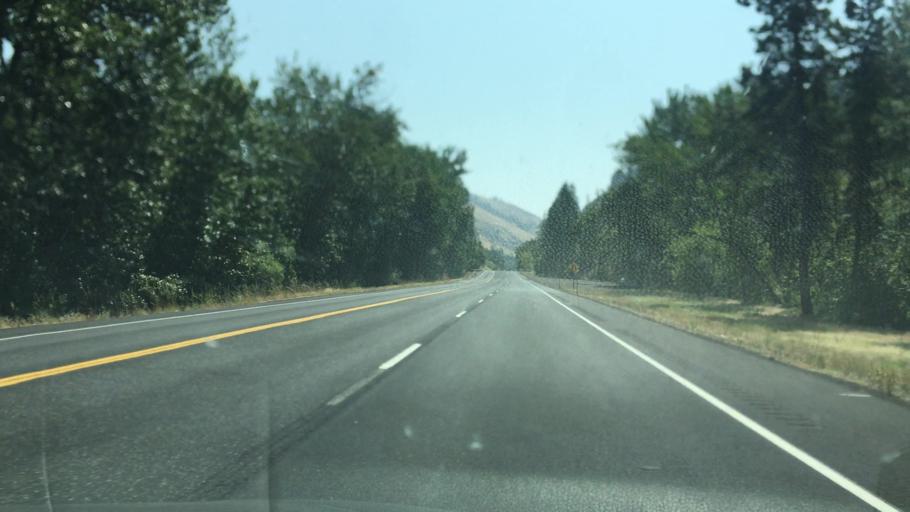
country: US
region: Idaho
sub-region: Nez Perce County
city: Lapwai
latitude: 46.3702
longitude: -116.6499
